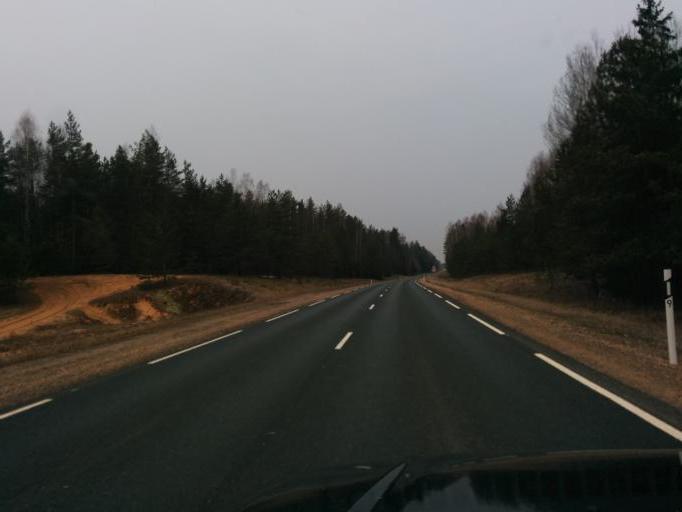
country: LV
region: Ikskile
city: Ikskile
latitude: 56.8032
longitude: 24.5021
